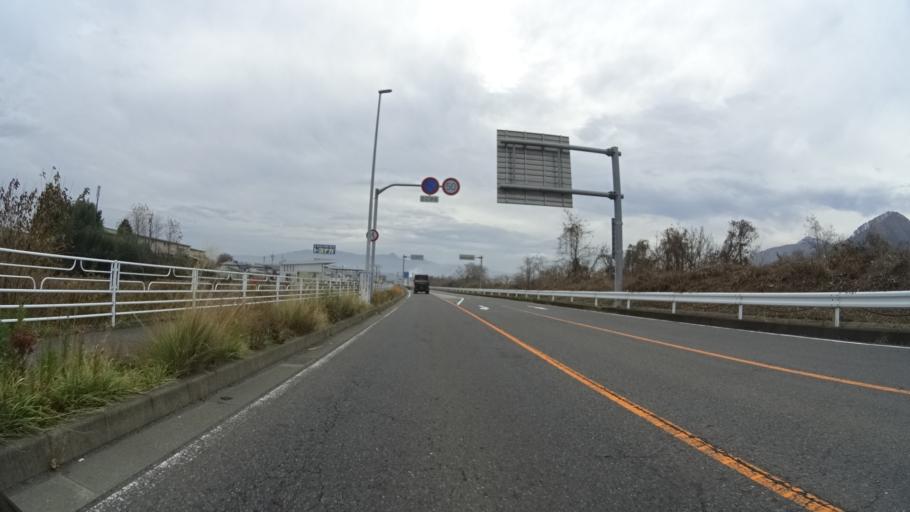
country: JP
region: Gunma
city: Numata
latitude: 36.6630
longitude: 139.0144
